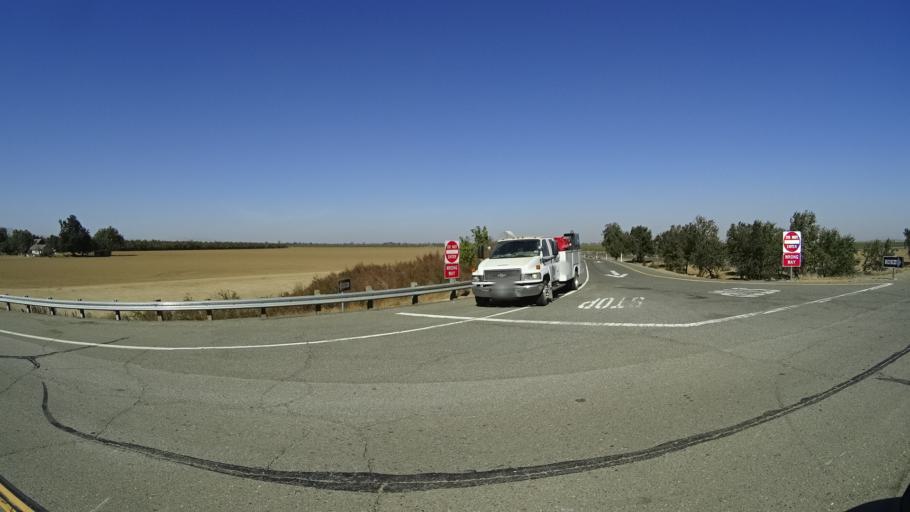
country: US
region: California
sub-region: Yolo County
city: Winters
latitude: 38.5838
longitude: -121.9544
